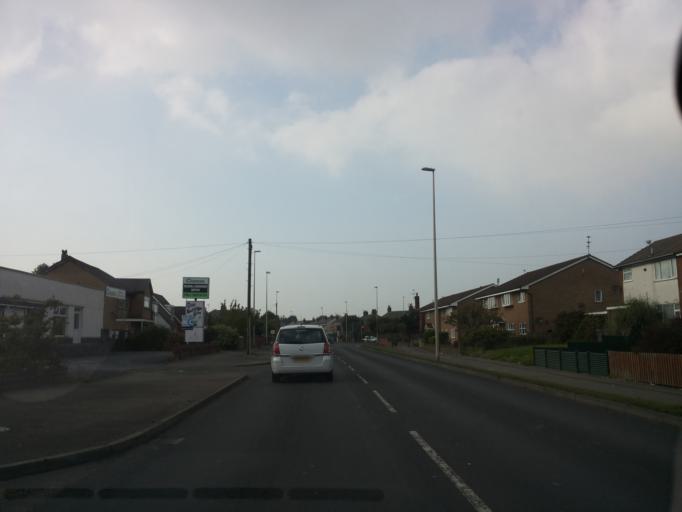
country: GB
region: England
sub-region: Lancashire
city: Great Marton
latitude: 53.8001
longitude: -3.0093
